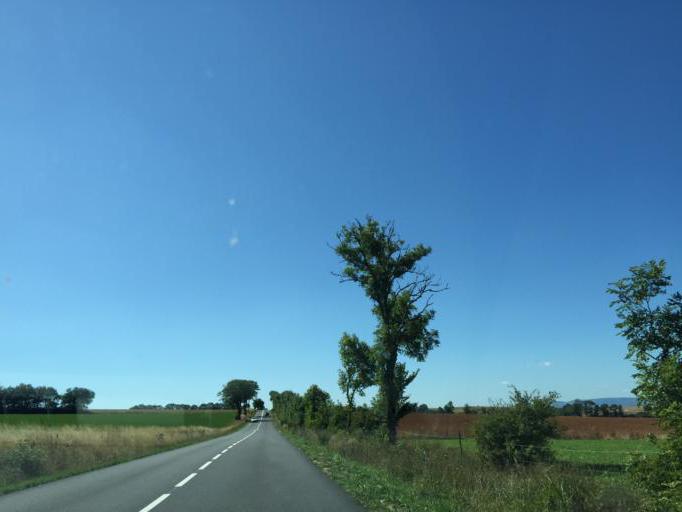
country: FR
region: Midi-Pyrenees
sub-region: Departement de l'Aveyron
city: La Cavalerie
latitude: 44.0153
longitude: 3.1055
